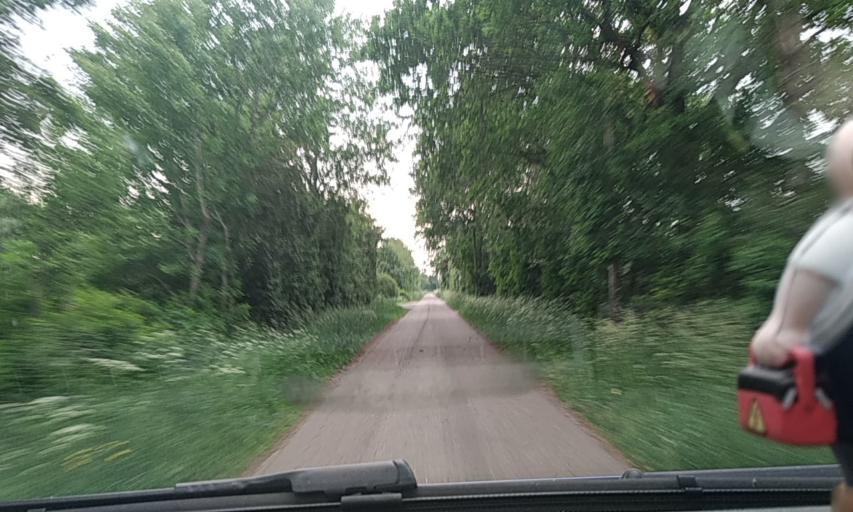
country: DE
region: Schleswig-Holstein
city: Borm
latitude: 54.3873
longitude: 9.3907
